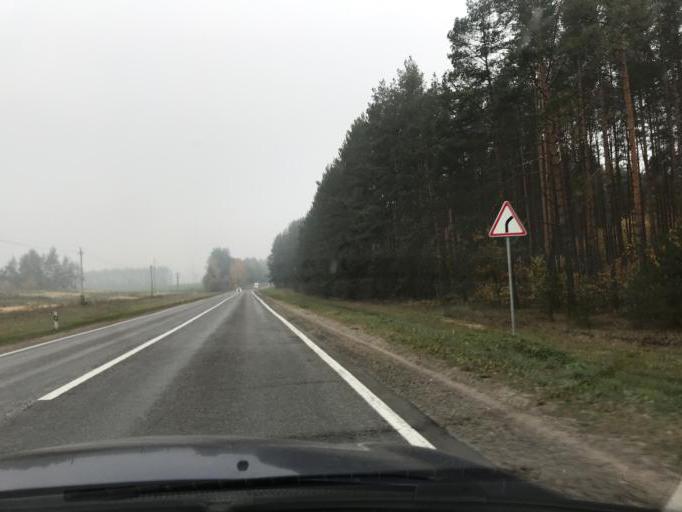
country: BY
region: Grodnenskaya
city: Hrodna
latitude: 53.7857
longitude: 23.8514
